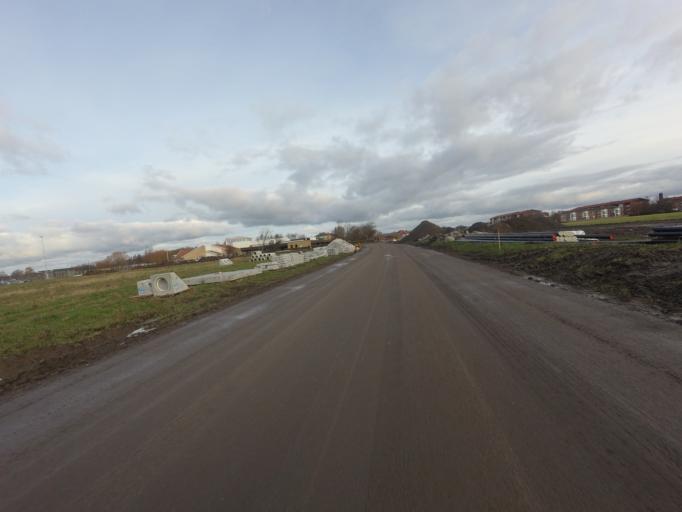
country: SE
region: Skane
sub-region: Hoganas Kommun
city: Hoganas
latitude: 56.1906
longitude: 12.5691
